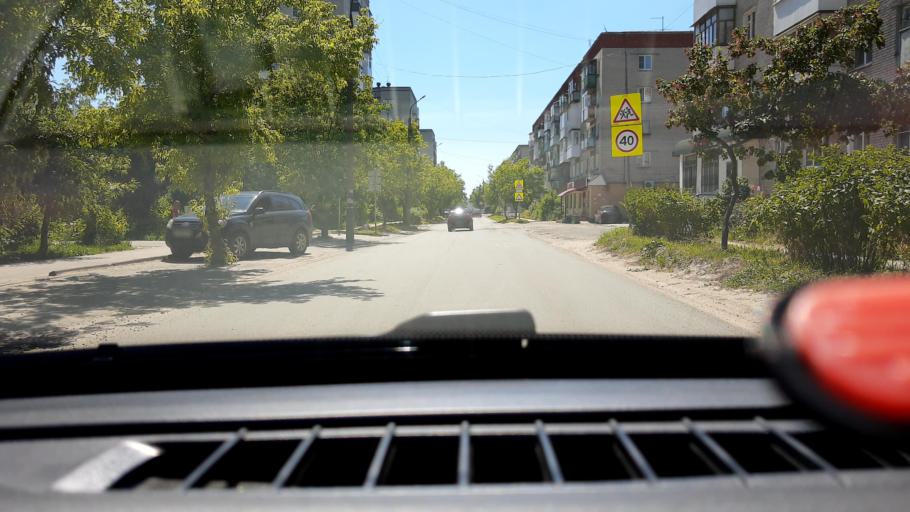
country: RU
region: Nizjnij Novgorod
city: Dzerzhinsk
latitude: 56.2536
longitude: 43.4745
